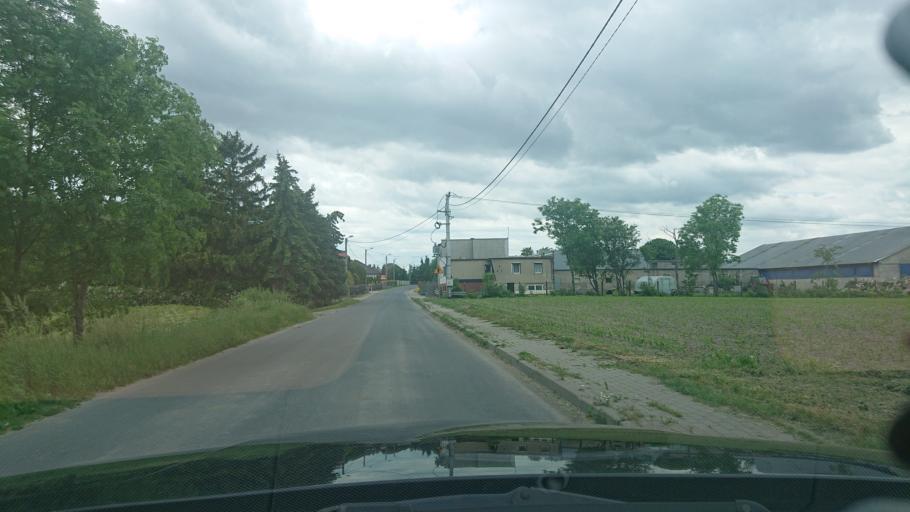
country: PL
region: Greater Poland Voivodeship
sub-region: Powiat gnieznienski
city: Gniezno
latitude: 52.5412
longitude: 17.5429
